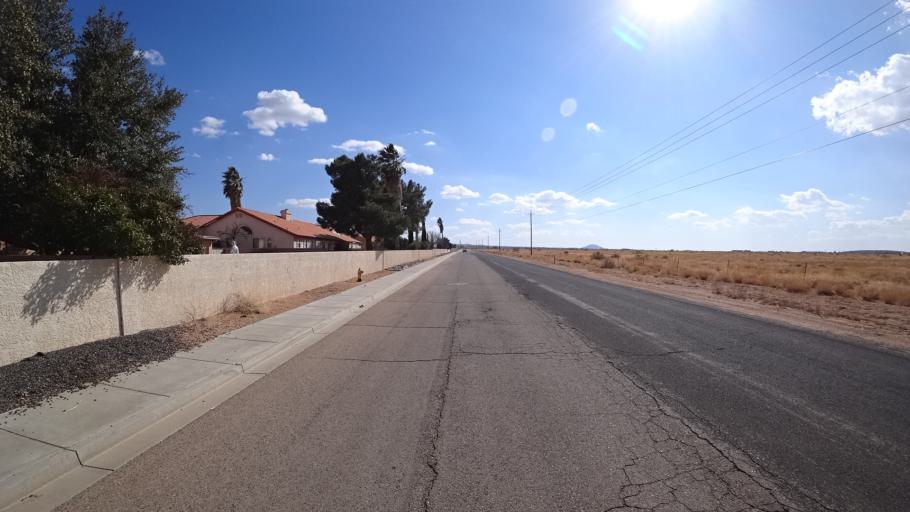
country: US
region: Arizona
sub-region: Mohave County
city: New Kingman-Butler
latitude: 35.2226
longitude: -113.9761
